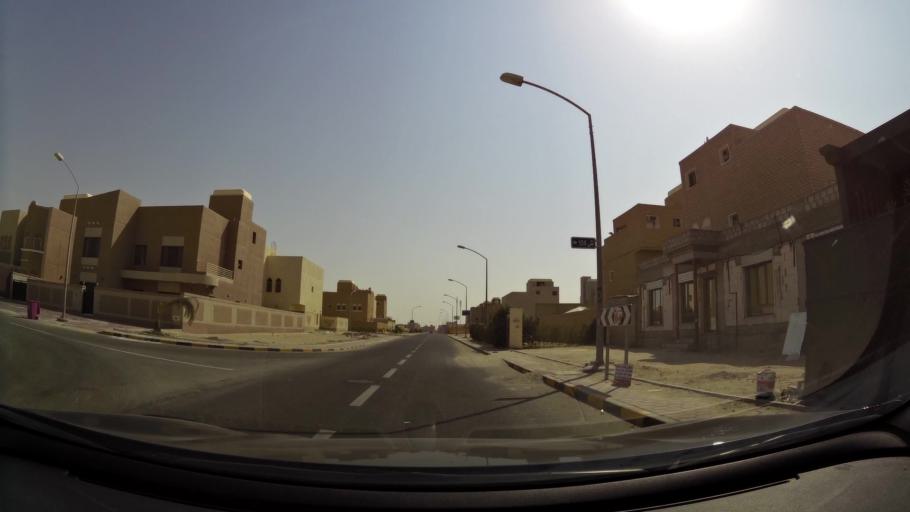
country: KW
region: Al Ahmadi
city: Al Wafrah
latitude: 28.8059
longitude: 48.0501
